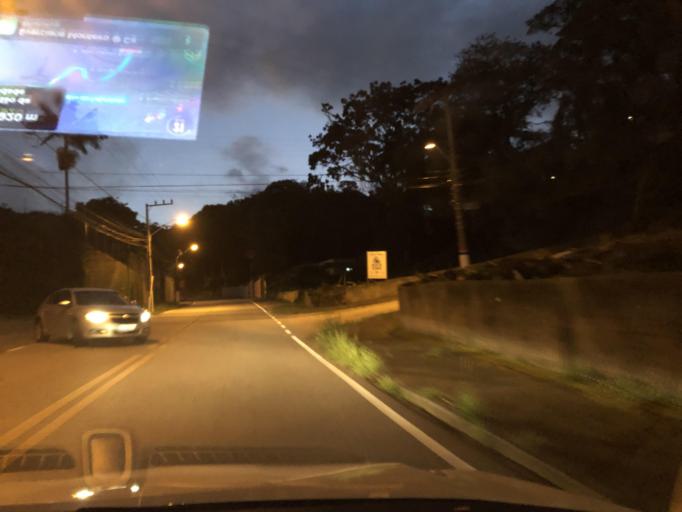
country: BR
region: Santa Catarina
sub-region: Florianopolis
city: Morro da Cruz
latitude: -27.5841
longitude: -48.5356
